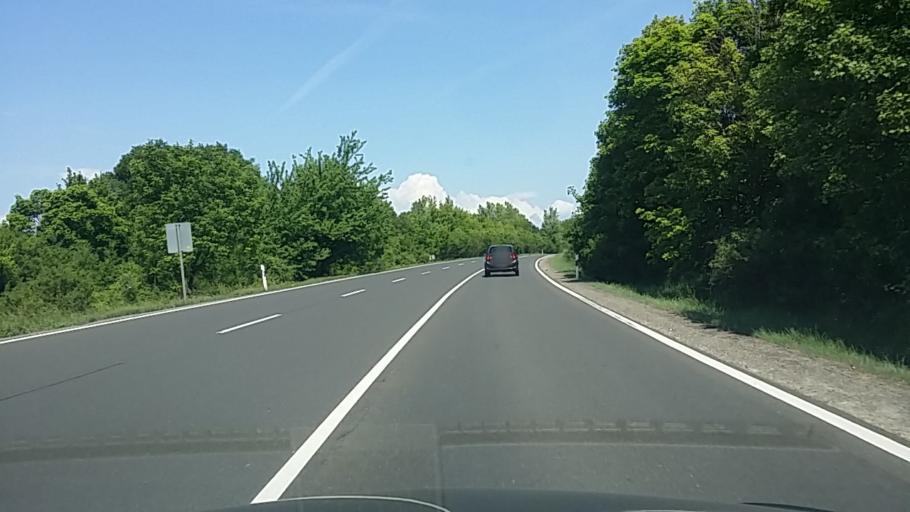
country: HU
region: Nograd
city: Nagyoroszi
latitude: 48.0322
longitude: 19.0589
